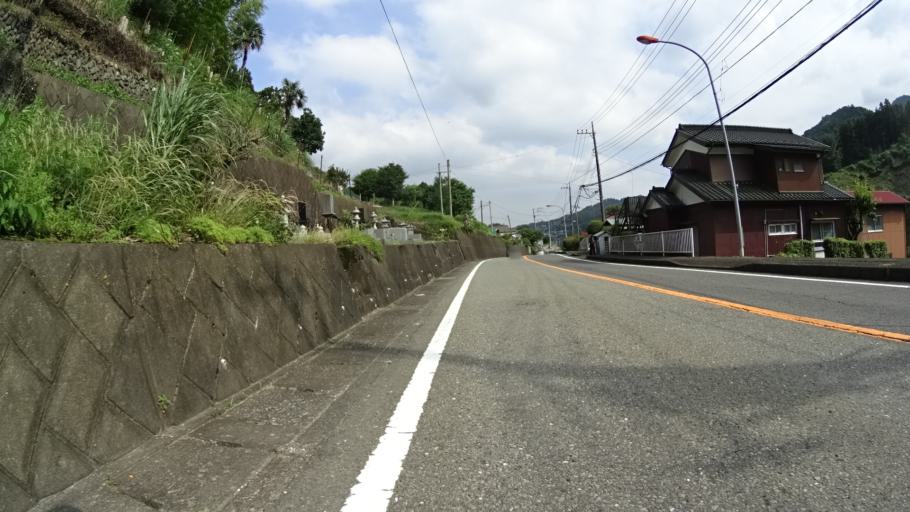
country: JP
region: Kanagawa
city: Atsugi
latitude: 35.4924
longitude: 139.2695
